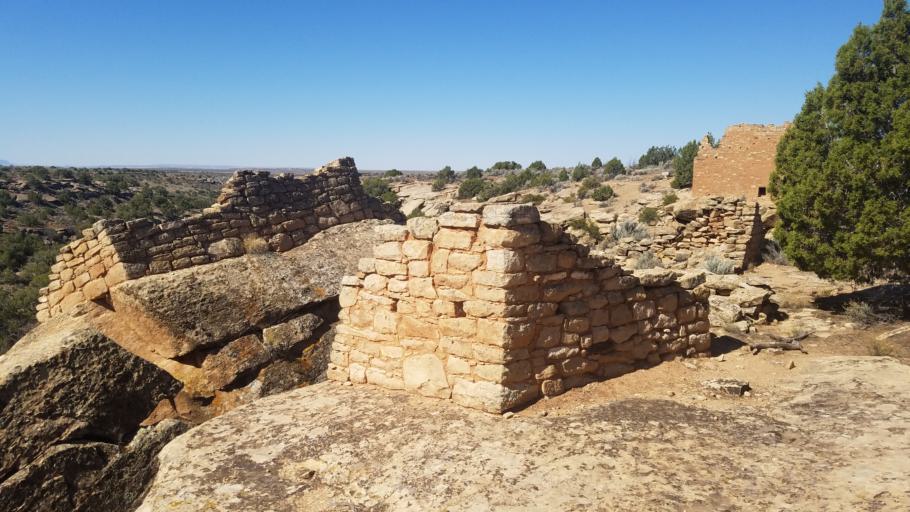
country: US
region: Colorado
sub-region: Montezuma County
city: Towaoc
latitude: 37.3997
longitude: -109.0413
